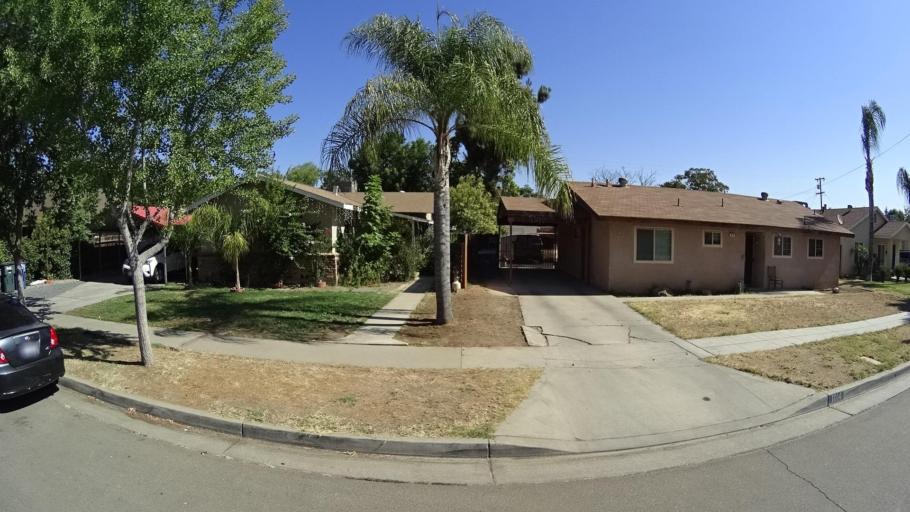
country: US
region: California
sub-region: Fresno County
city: Fresno
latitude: 36.7766
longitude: -119.8236
